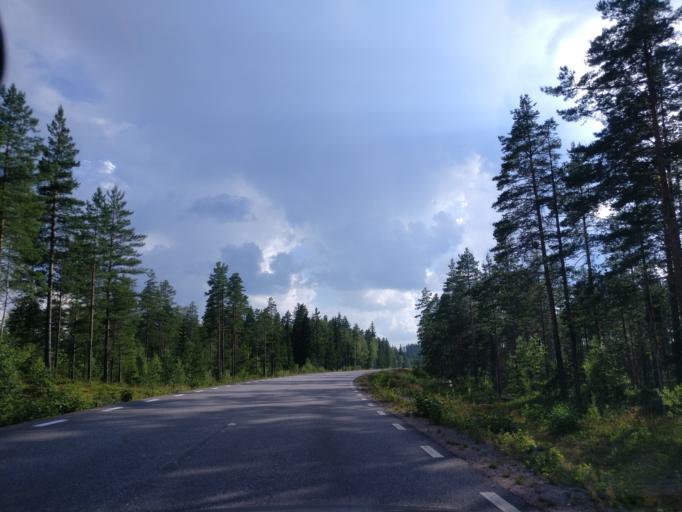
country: SE
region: Dalarna
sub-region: Ludvika Kommun
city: Abborrberget
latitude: 60.1842
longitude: 14.7188
